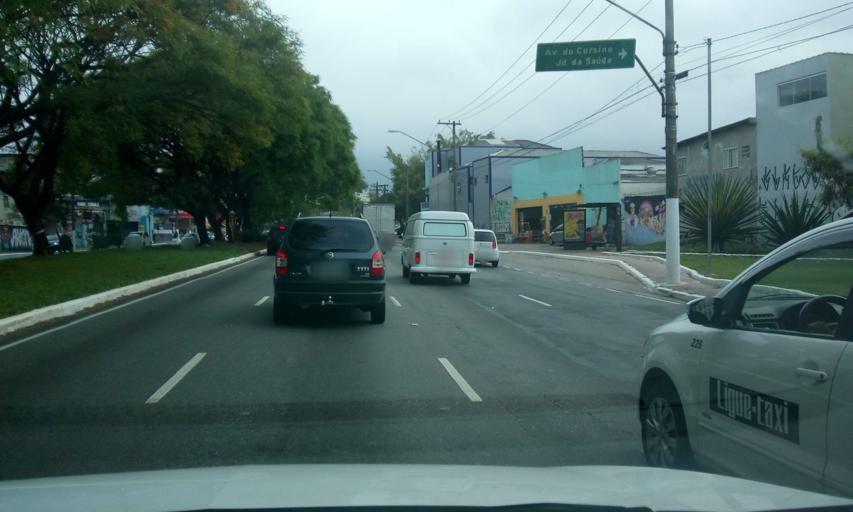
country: BR
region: Sao Paulo
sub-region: Sao Caetano Do Sul
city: Sao Caetano do Sul
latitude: -23.6211
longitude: -46.6118
